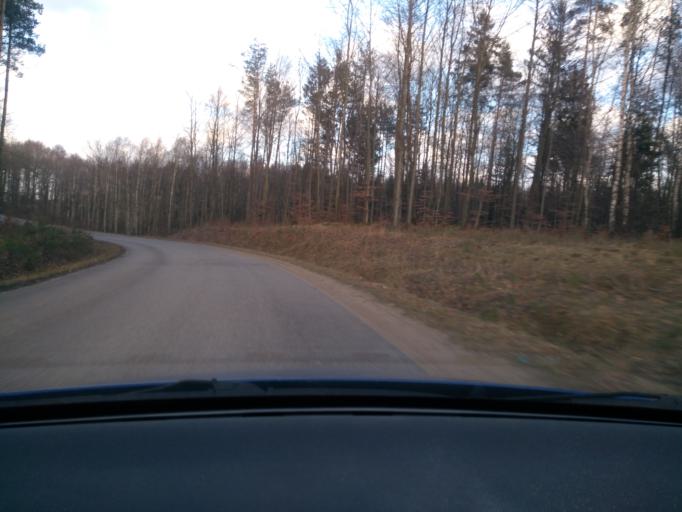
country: PL
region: Pomeranian Voivodeship
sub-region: Powiat kartuski
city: Kartuzy
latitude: 54.3672
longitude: 18.2193
